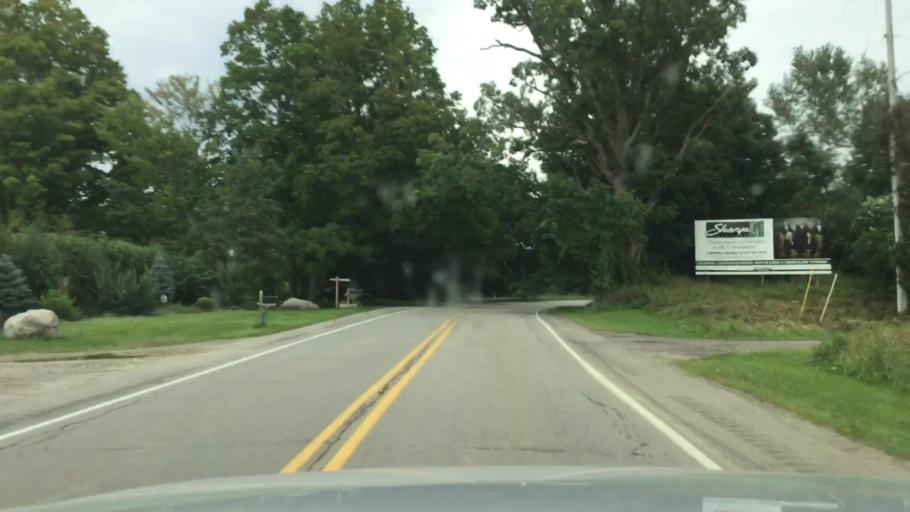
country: US
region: Michigan
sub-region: Genesee County
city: Argentine
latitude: 42.7995
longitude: -83.8625
